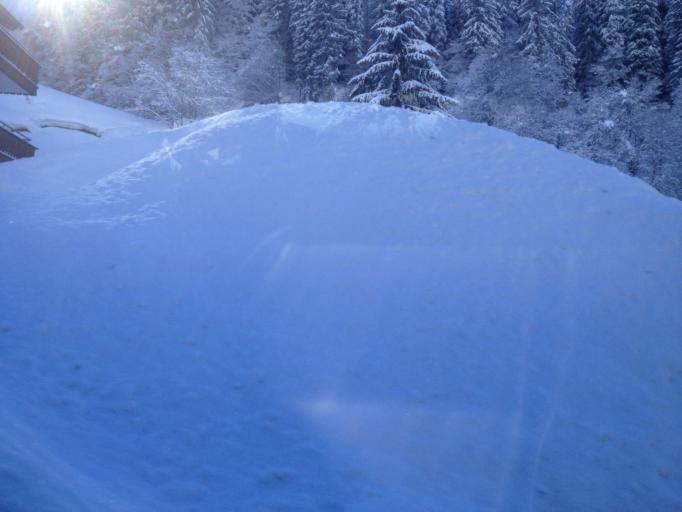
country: CH
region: Grisons
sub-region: Praettigau/Davos District
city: Klosters Serneus
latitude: 46.8612
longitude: 9.8965
